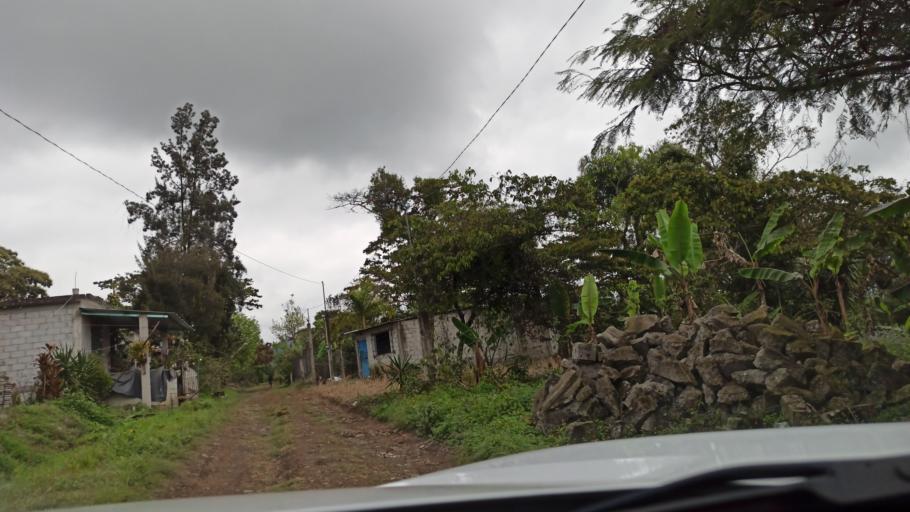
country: MX
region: Veracruz
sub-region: Chocaman
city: San Jose Neria
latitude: 19.0083
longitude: -97.0098
